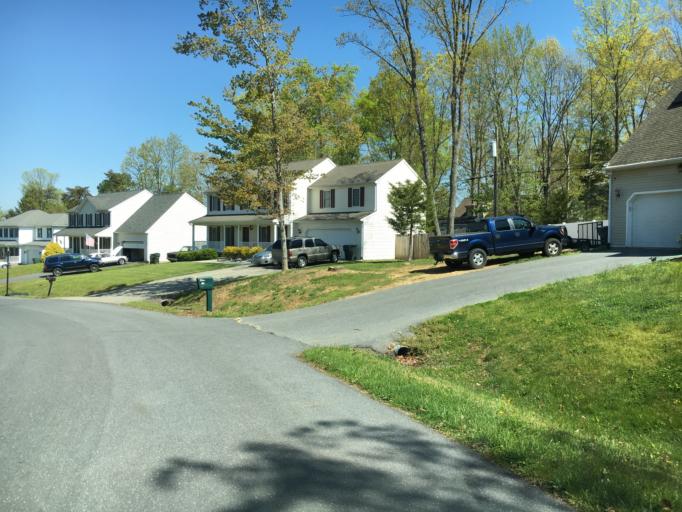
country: US
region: Virginia
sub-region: Augusta County
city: Crimora
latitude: 38.1381
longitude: -78.8391
